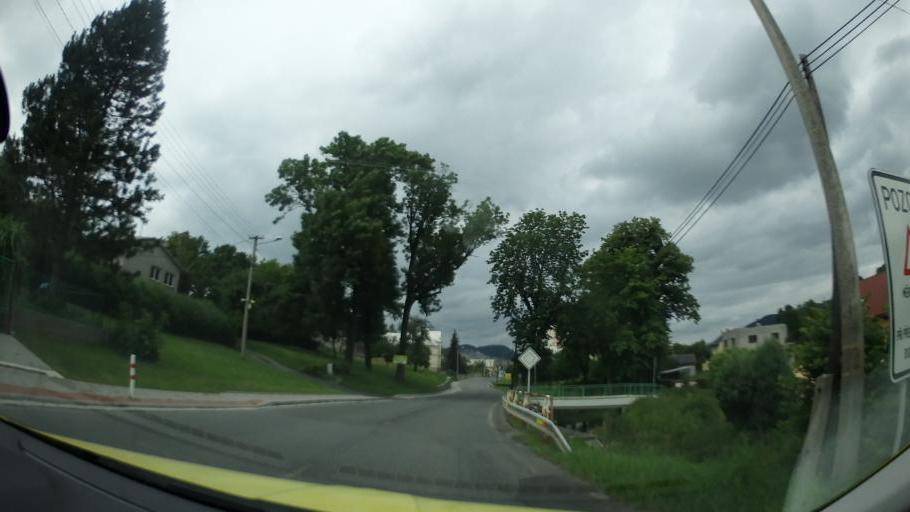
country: CZ
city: Verovice
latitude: 49.5618
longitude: 18.1067
